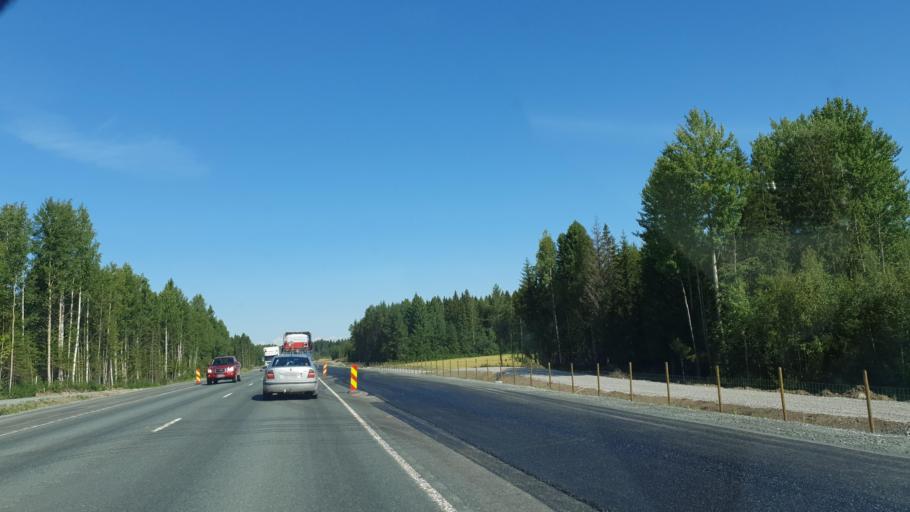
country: FI
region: Northern Savo
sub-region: Ylae-Savo
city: Lapinlahti
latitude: 63.2915
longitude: 27.4539
